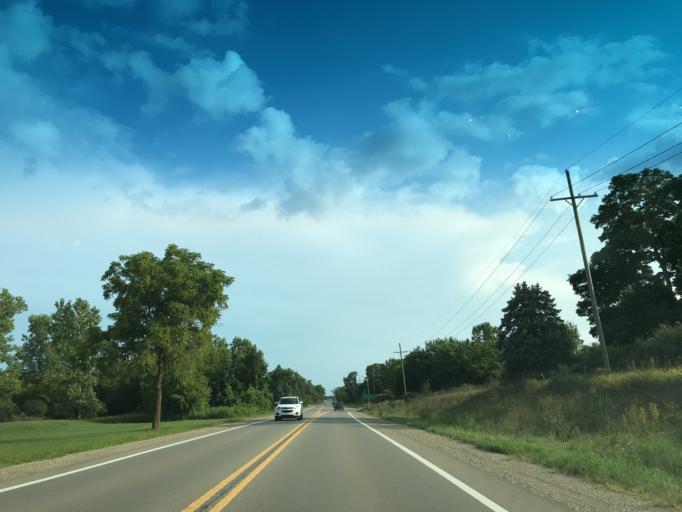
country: US
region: Michigan
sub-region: Oakland County
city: Milford
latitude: 42.5319
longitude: -83.6166
